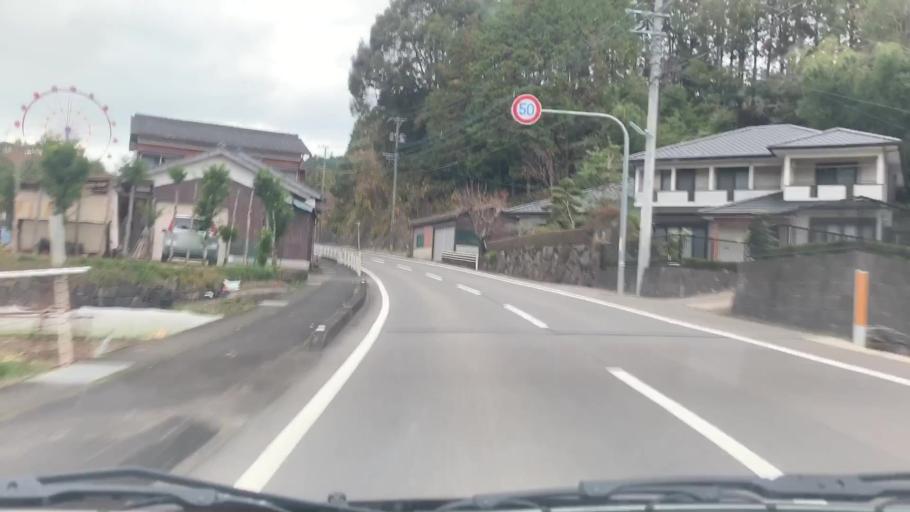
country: JP
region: Saga Prefecture
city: Ureshinomachi-shimojuku
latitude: 33.1288
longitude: 129.9791
